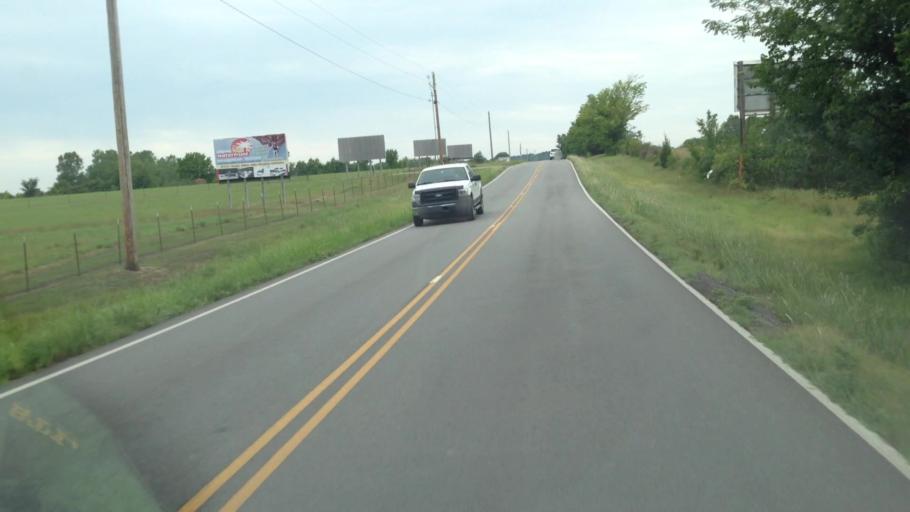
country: US
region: Oklahoma
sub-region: Delaware County
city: Cleora
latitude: 36.5682
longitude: -94.9791
